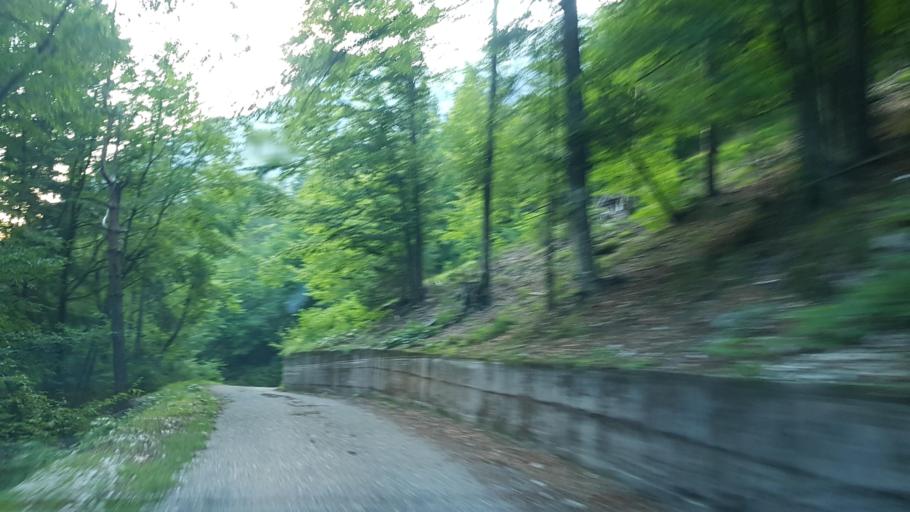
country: IT
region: Friuli Venezia Giulia
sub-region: Provincia di Udine
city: Malborghetto
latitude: 46.3997
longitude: 13.4309
